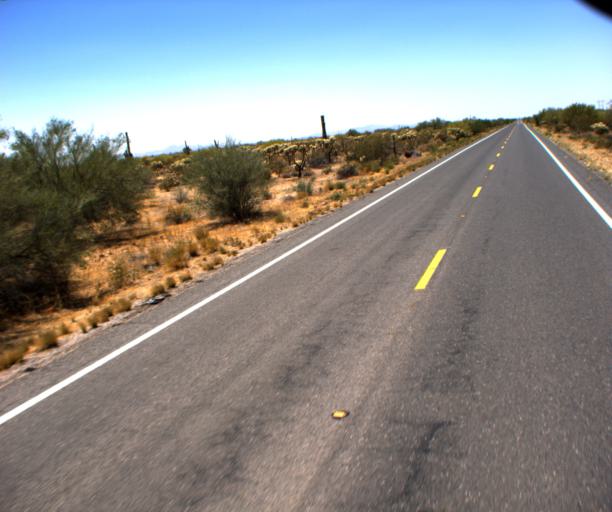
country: US
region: Arizona
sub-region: Pinal County
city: Florence
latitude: 32.8762
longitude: -111.2552
